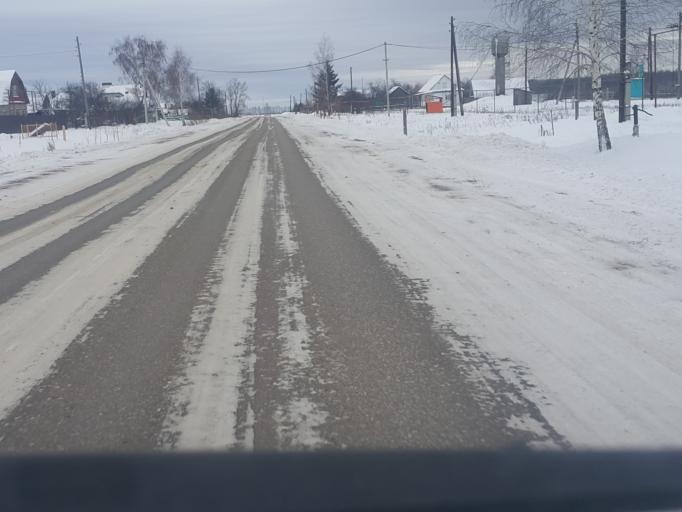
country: RU
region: Tambov
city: Platonovka
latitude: 52.8322
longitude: 41.8092
